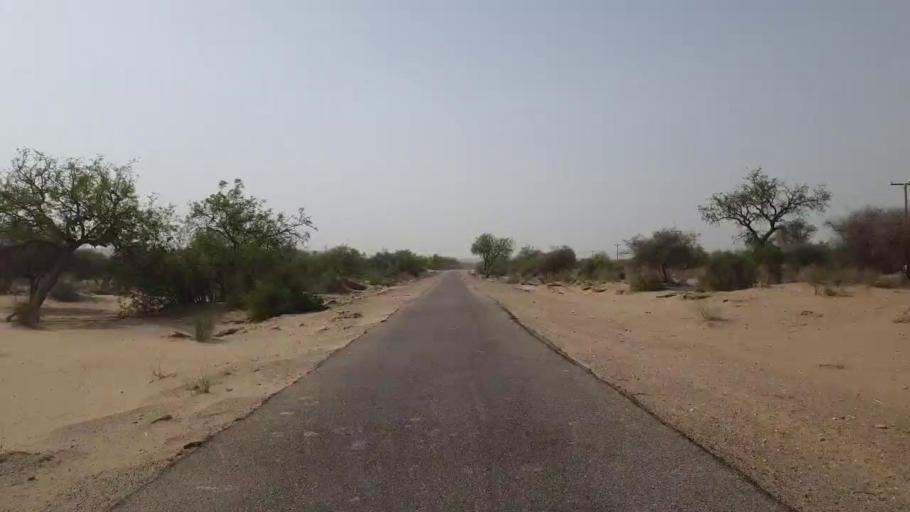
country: PK
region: Sindh
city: Mithi
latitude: 24.6032
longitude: 69.9226
